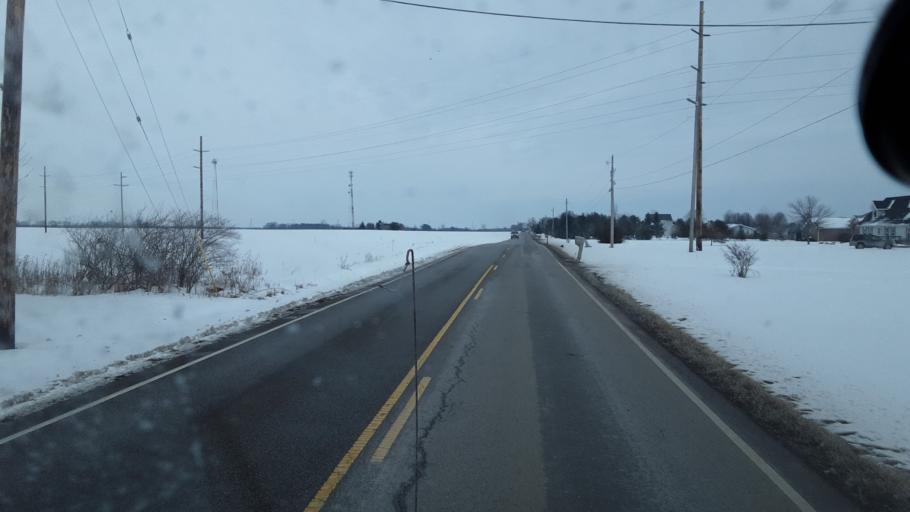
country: US
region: Ohio
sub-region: Union County
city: New California
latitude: 40.2160
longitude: -83.1770
